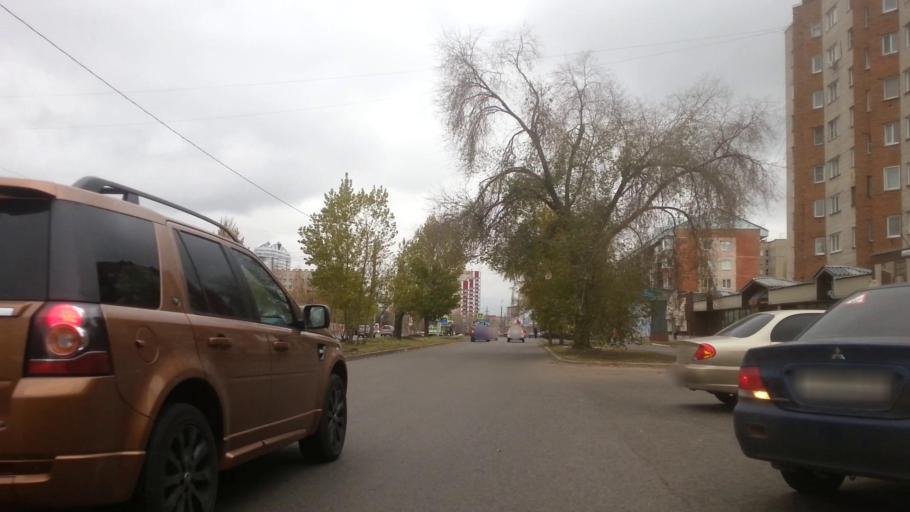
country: RU
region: Altai Krai
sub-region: Gorod Barnaulskiy
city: Barnaul
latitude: 53.3654
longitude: 83.7059
